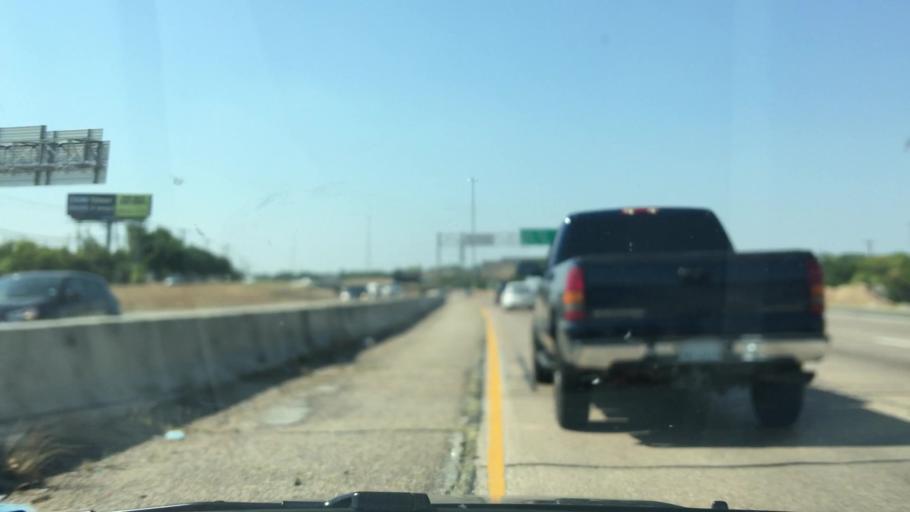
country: US
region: Texas
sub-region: Dallas County
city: Cockrell Hill
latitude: 32.7085
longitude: -96.8235
